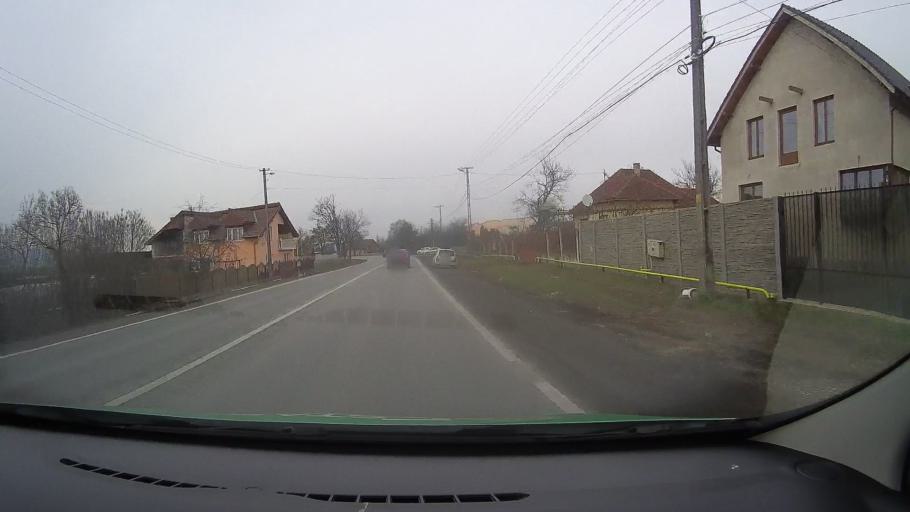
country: RO
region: Hunedoara
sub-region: Oras Simeria
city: Simeria
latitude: 45.8461
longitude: 23.0049
